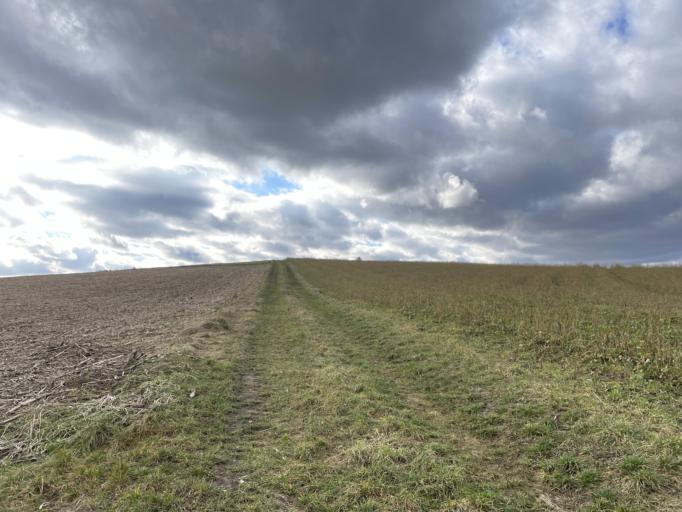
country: DE
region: Bavaria
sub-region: Upper Palatinate
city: Runding
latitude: 49.2291
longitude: 12.7637
